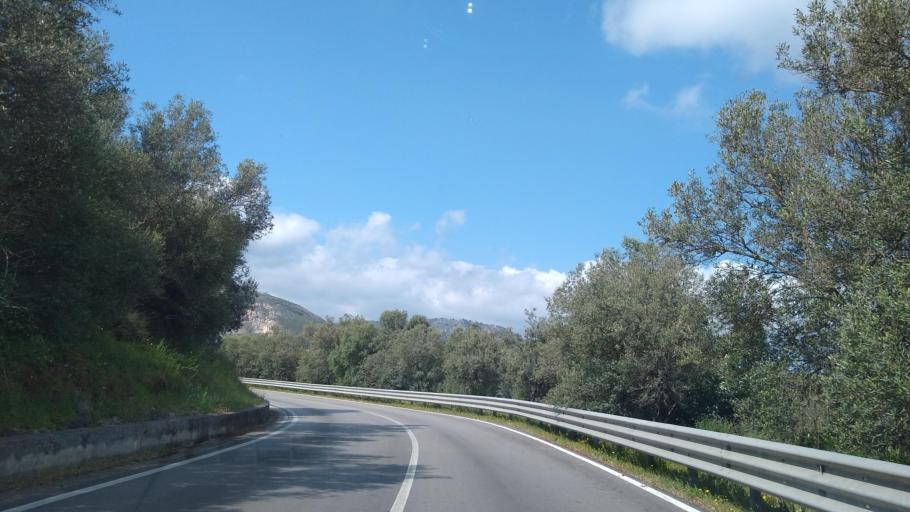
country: IT
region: Sicily
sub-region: Trapani
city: Calatafimi
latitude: 37.9550
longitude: 12.8661
